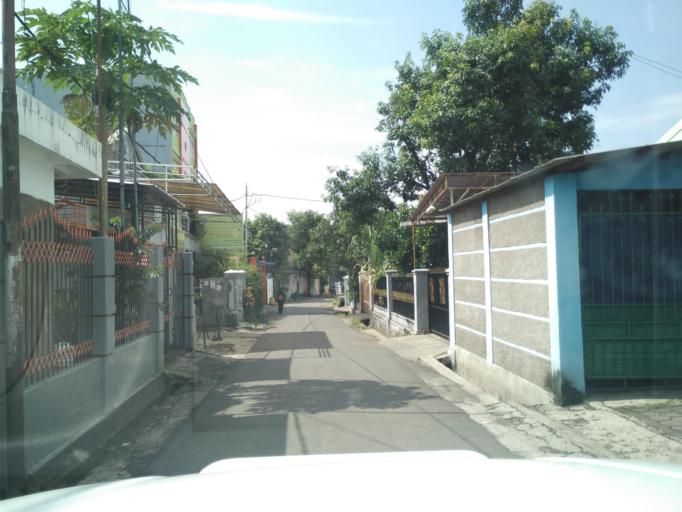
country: ID
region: West Java
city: Ciranjang-hilir
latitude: -6.8178
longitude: 107.1458
